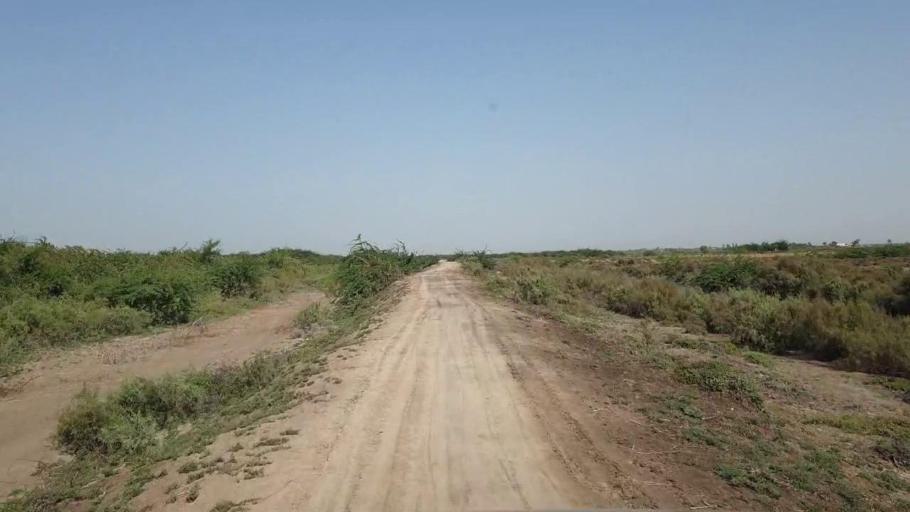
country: PK
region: Sindh
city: Tando Bago
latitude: 24.6534
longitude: 69.0706
